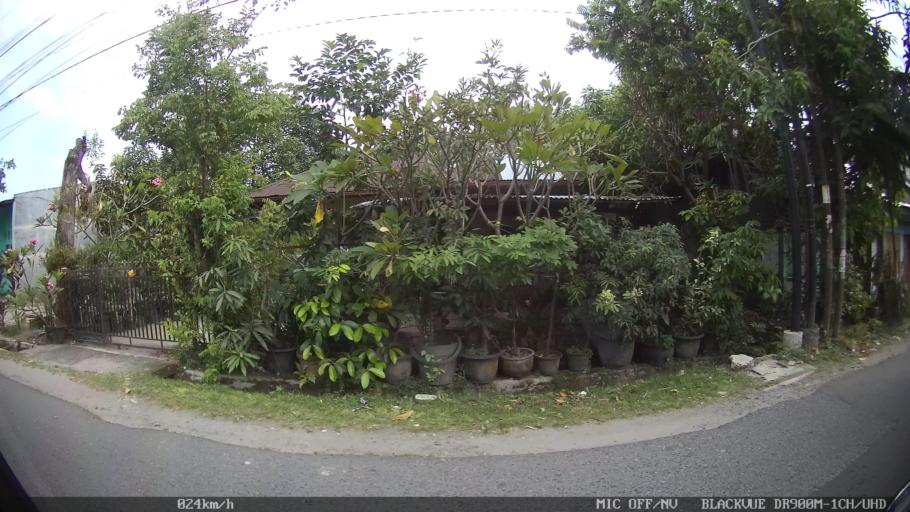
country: ID
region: North Sumatra
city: Medan
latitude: 3.5558
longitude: 98.6864
